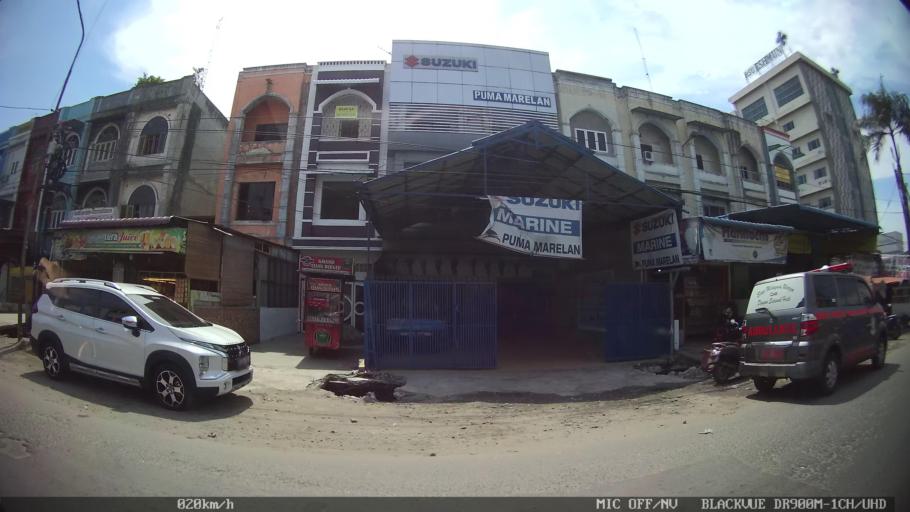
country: ID
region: North Sumatra
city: Labuhan Deli
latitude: 3.6870
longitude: 98.6560
